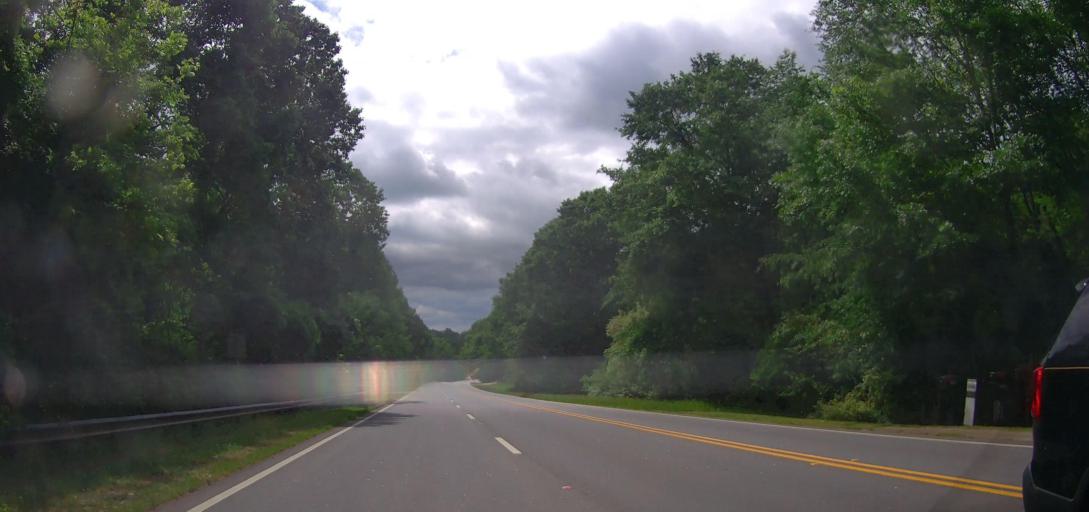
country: US
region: Georgia
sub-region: Rockdale County
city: Conyers
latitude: 33.6205
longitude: -84.0646
